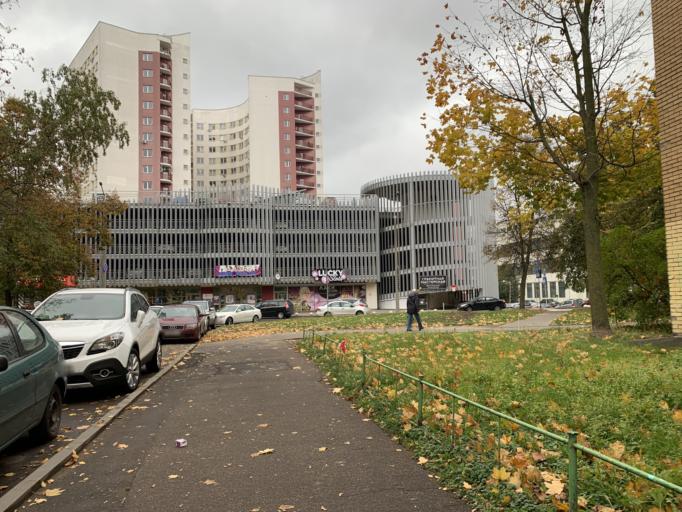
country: BY
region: Minsk
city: Minsk
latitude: 53.9382
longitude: 27.6007
